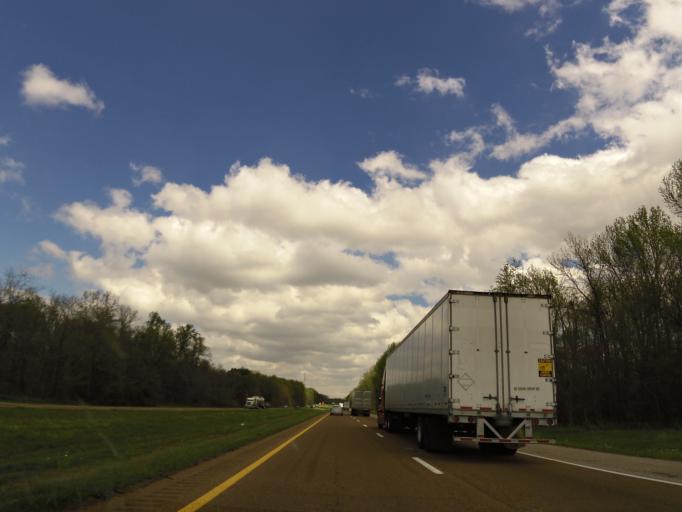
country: US
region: Tennessee
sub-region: Tipton County
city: Mason
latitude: 35.3662
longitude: -89.4803
